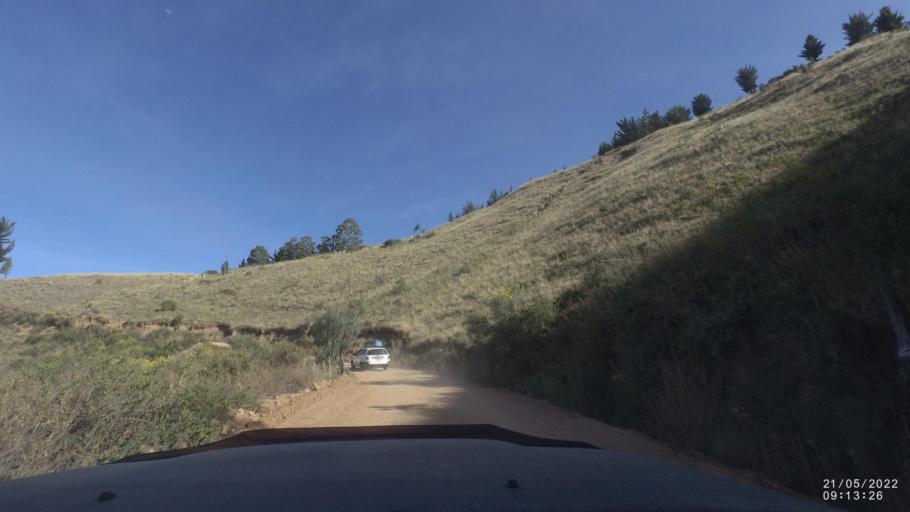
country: BO
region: Cochabamba
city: Cochabamba
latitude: -17.3662
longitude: -66.0261
